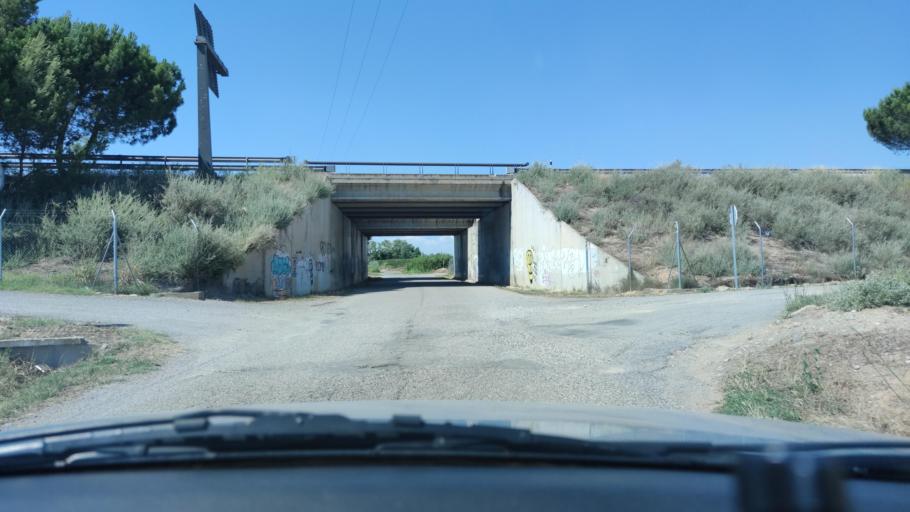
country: ES
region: Catalonia
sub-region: Provincia de Lleida
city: Torrefarrera
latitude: 41.6635
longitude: 0.6197
